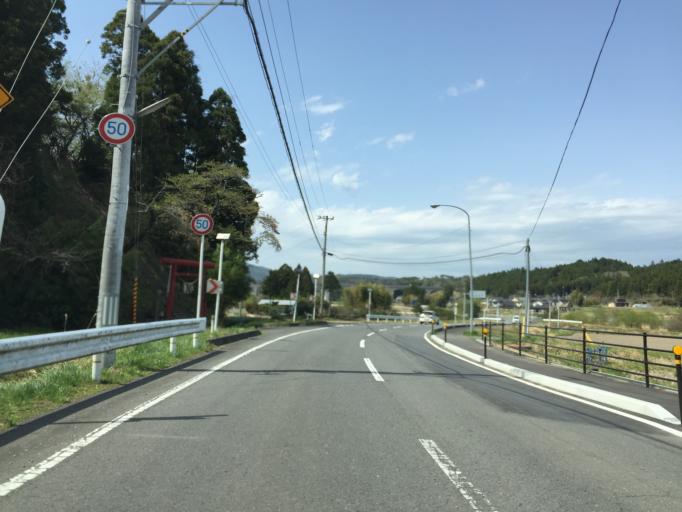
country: JP
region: Fukushima
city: Iwaki
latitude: 37.1628
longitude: 140.9725
